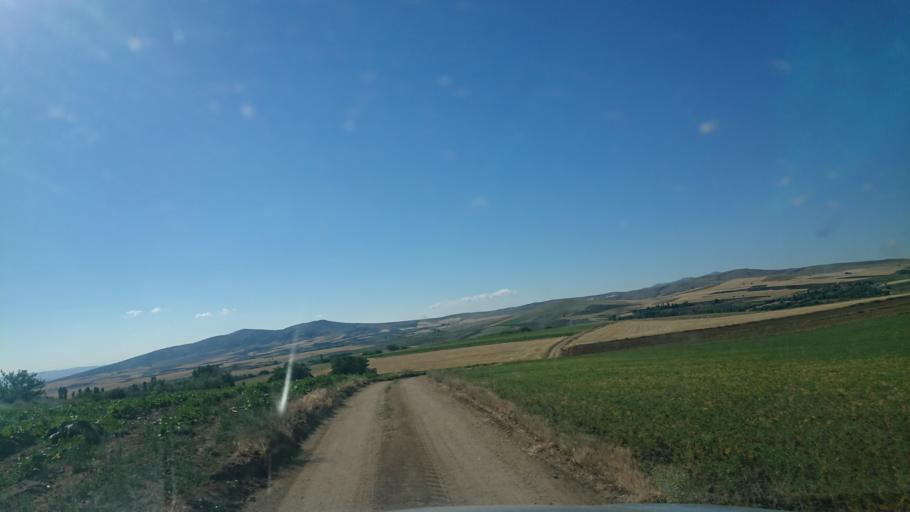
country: TR
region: Aksaray
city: Agacoren
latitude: 38.8314
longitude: 33.9513
